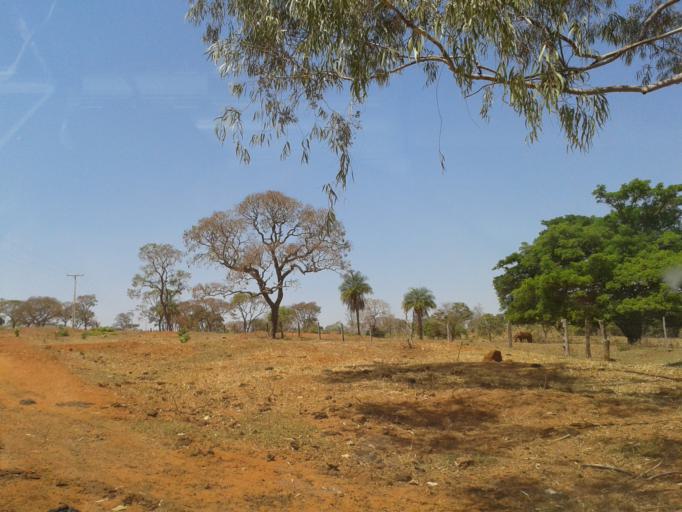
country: BR
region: Minas Gerais
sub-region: Ituiutaba
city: Ituiutaba
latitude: -19.0684
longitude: -49.3697
